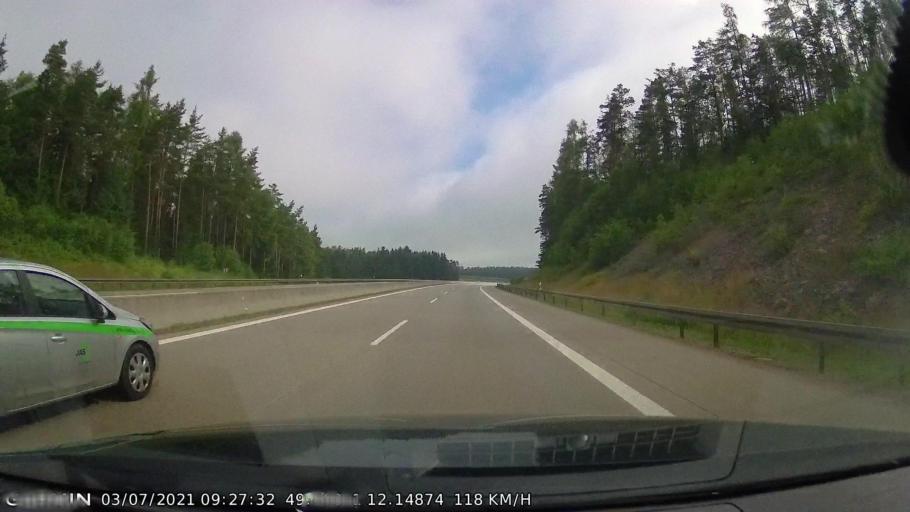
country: DE
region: Bavaria
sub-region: Upper Palatinate
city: Pfreimd
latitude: 49.4983
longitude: 12.1487
